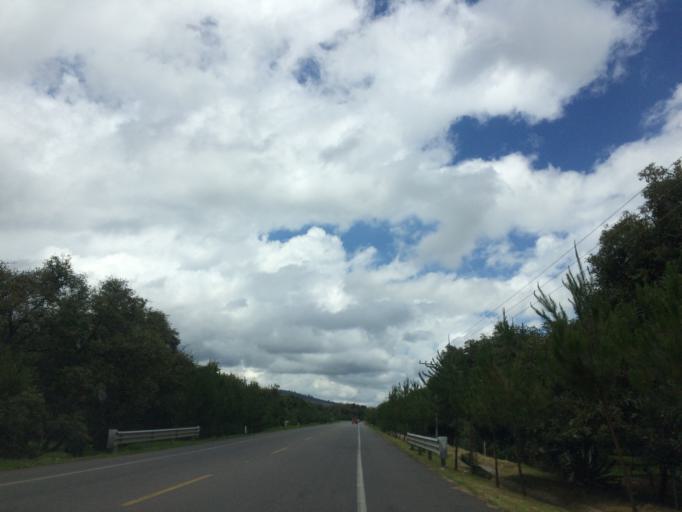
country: MX
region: Michoacan
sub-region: Uruapan
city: Santa Ana Zirosto
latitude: 19.5444
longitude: -102.3213
